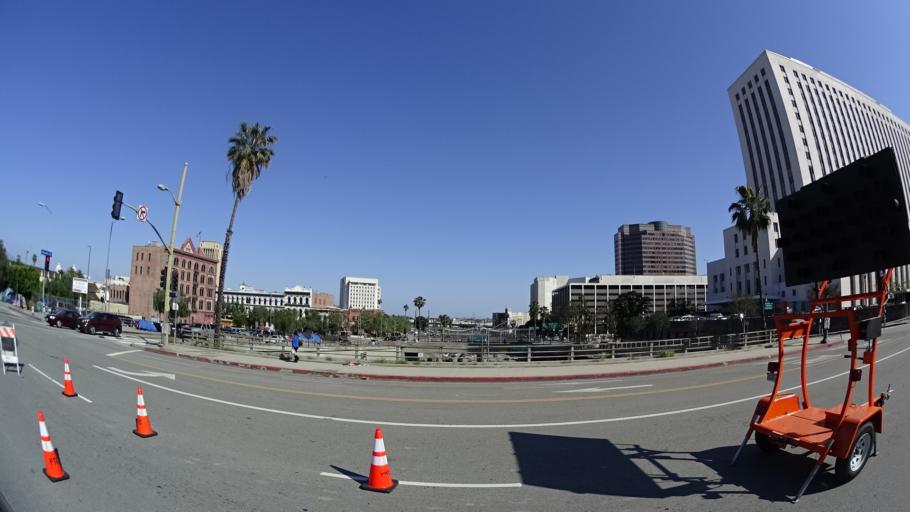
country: US
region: California
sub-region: Los Angeles County
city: Los Angeles
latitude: 34.0564
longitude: -118.2412
